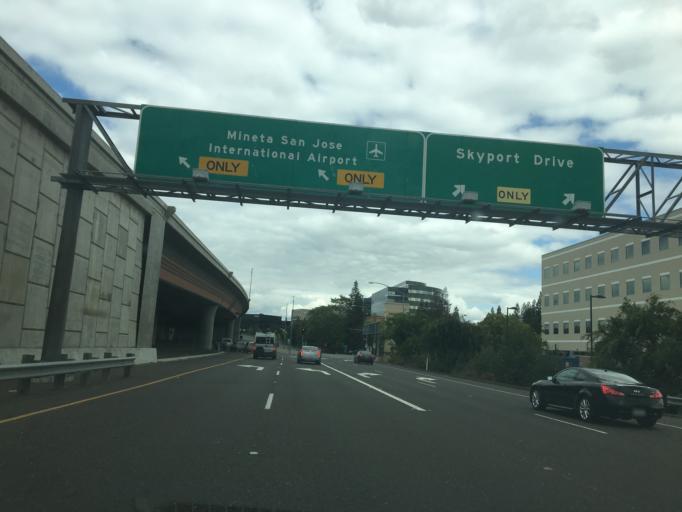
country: US
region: California
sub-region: Santa Clara County
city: San Jose
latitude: 37.3635
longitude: -121.9179
